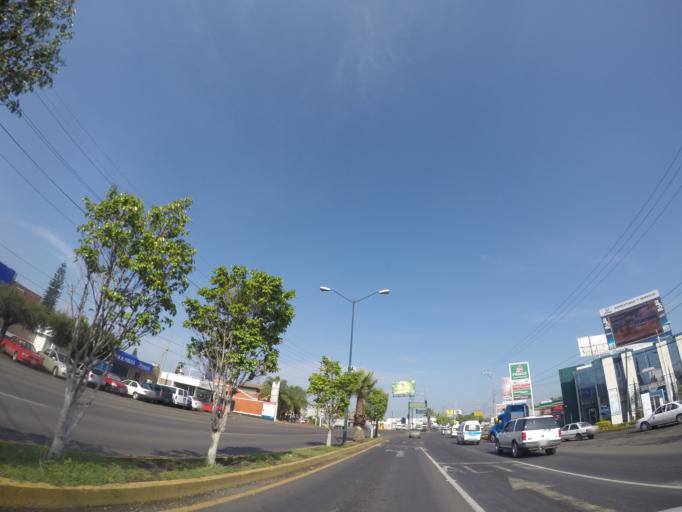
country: MX
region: Michoacan
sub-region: Morelia
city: Morelos
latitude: 19.6770
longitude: -101.2292
